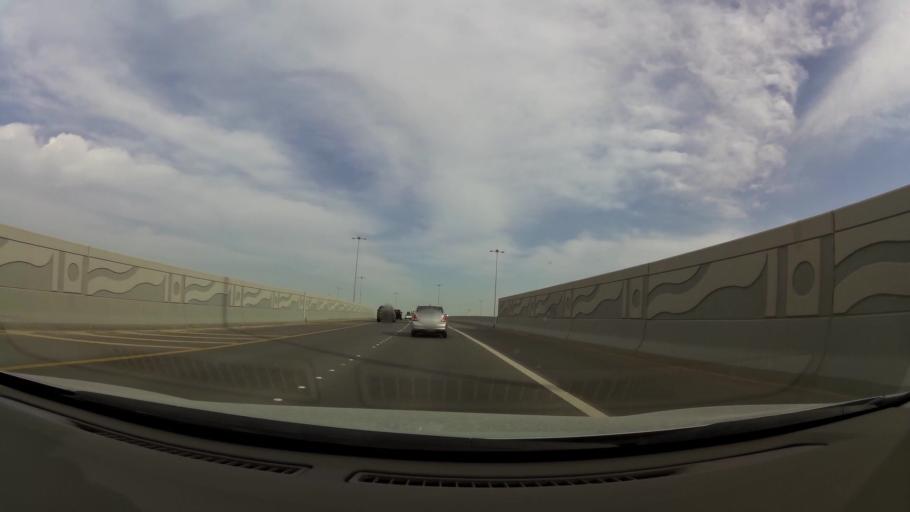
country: QA
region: Baladiyat ad Dawhah
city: Doha
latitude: 25.2555
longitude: 51.5049
